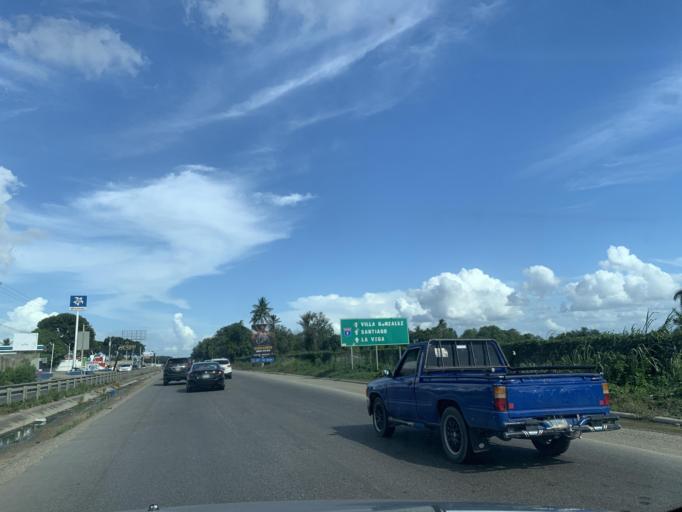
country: DO
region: Santiago
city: Villa Gonzalez
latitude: 19.5439
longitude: -70.8022
